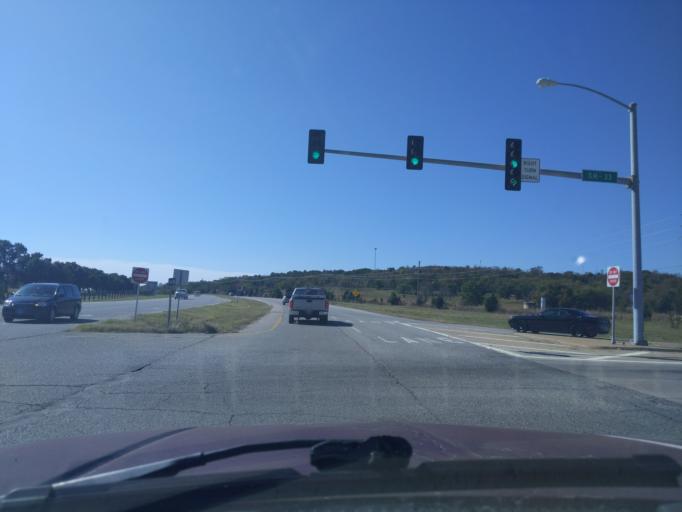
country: US
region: Oklahoma
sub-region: Creek County
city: Kellyville
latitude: 35.9858
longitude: -96.1912
